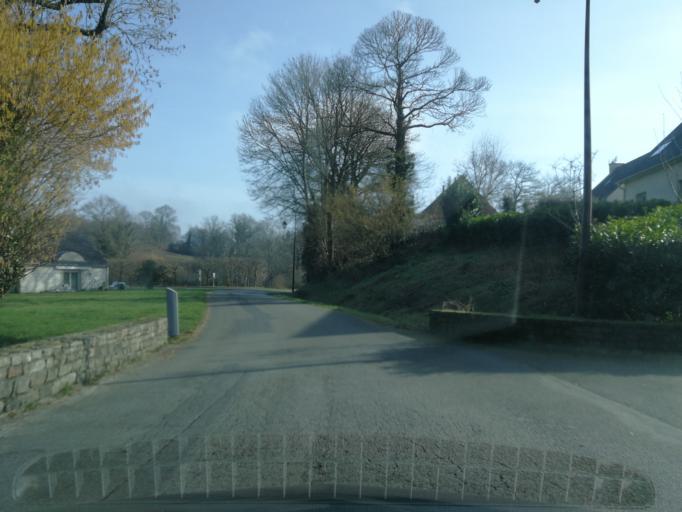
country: FR
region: Brittany
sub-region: Departement du Morbihan
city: La Vraie-Croix
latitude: 47.7104
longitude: -2.5158
